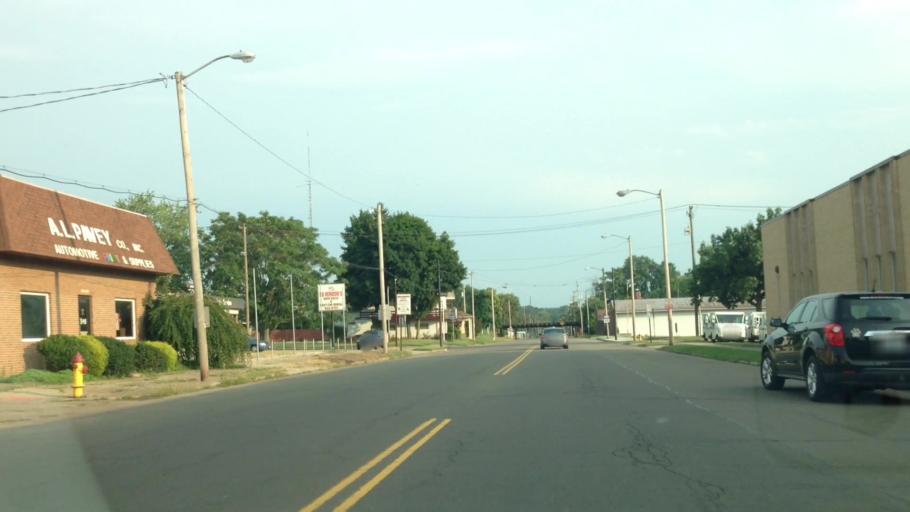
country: US
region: Ohio
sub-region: Stark County
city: Massillon
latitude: 40.7935
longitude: -81.5218
